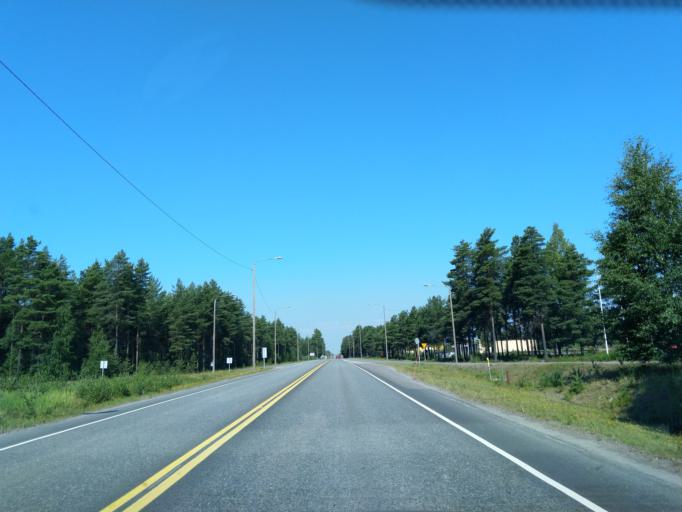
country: FI
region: Satakunta
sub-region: Pori
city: Harjavalta
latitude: 61.3069
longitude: 22.1273
